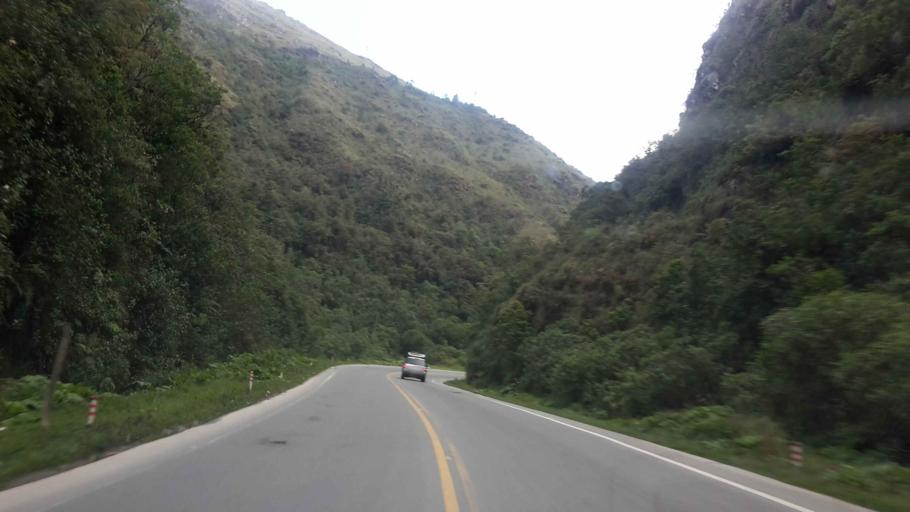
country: BO
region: Cochabamba
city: Colomi
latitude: -17.2101
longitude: -65.8887
